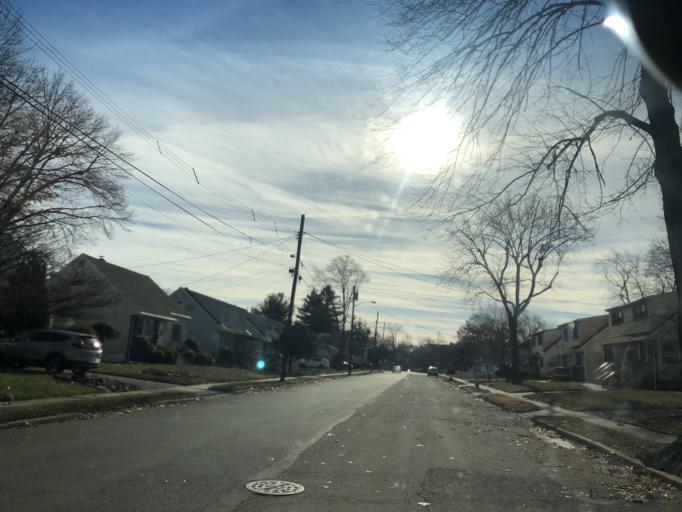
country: US
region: New Jersey
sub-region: Bergen County
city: Fair Lawn
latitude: 40.9278
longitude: -74.1374
